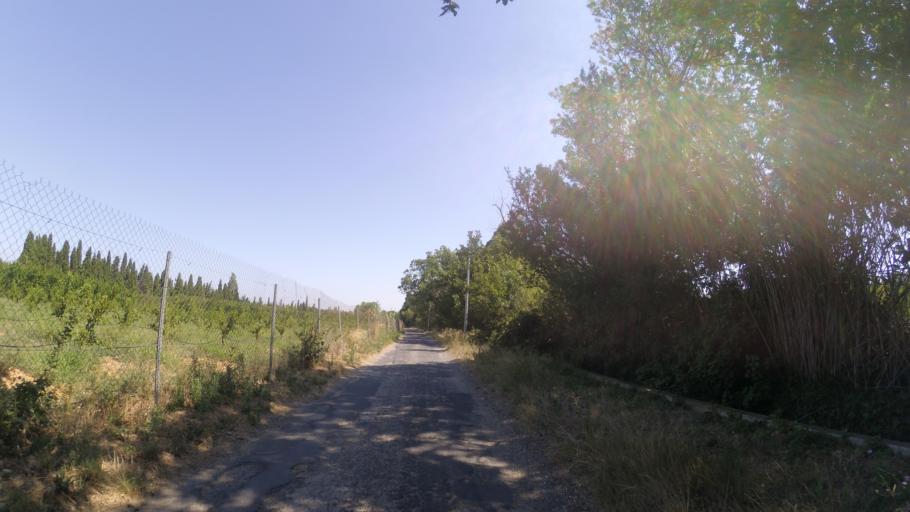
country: FR
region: Languedoc-Roussillon
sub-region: Departement des Pyrenees-Orientales
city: Corneilla-la-Riviere
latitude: 42.6645
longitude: 2.7254
